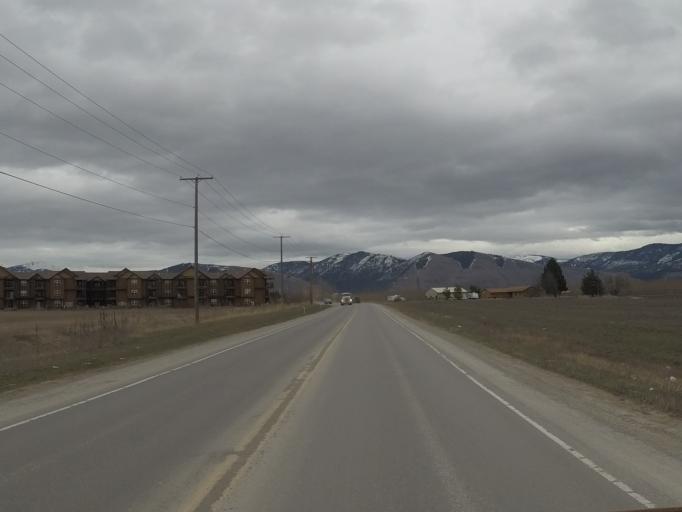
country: US
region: Montana
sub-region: Missoula County
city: Orchard Homes
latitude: 46.8868
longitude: -114.0525
